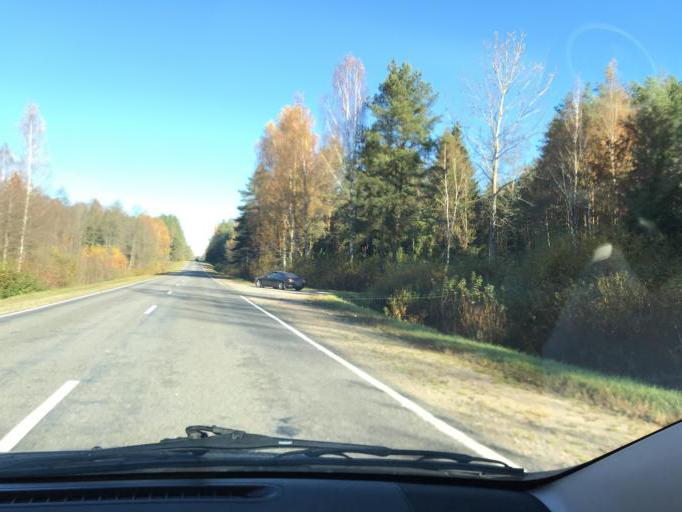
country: BY
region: Vitebsk
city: Lyepyel'
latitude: 54.9528
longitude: 28.7424
